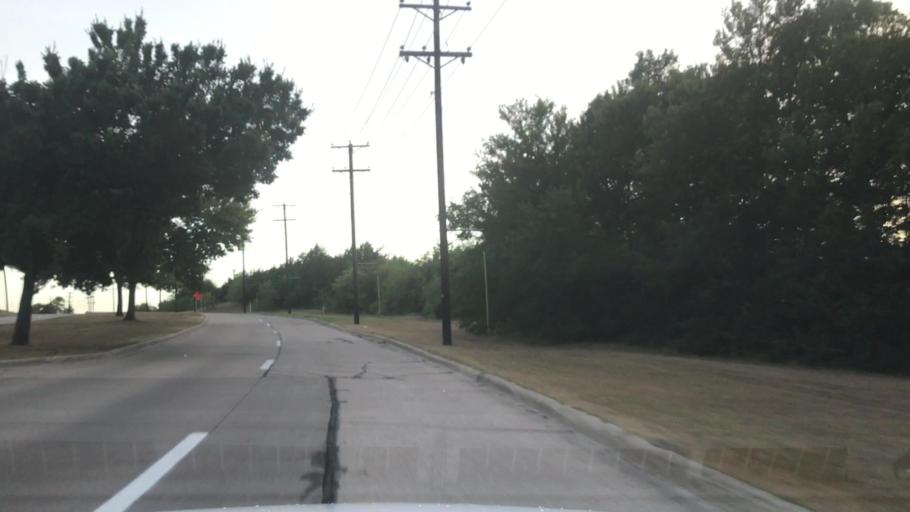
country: US
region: Texas
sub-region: Dallas County
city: Balch Springs
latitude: 32.7069
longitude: -96.5650
